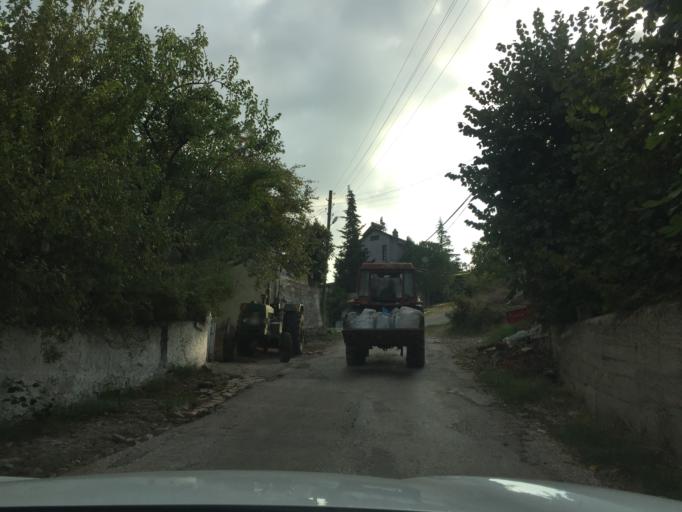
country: TR
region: Balikesir
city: Gonen
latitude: 40.0503
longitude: 27.5846
